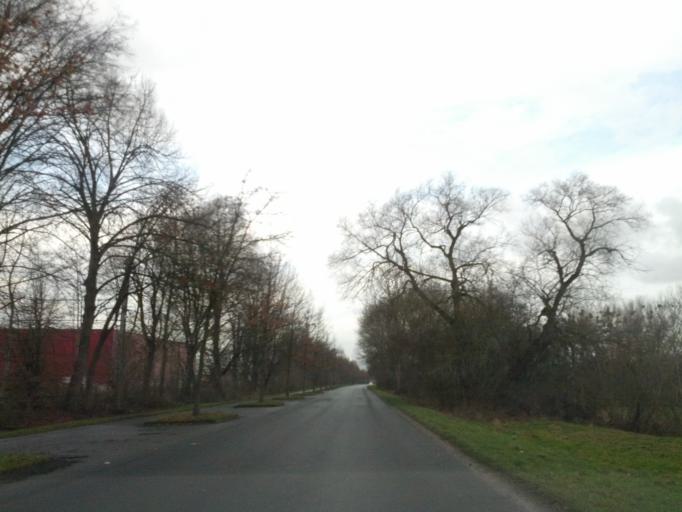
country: DE
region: Hesse
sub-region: Regierungsbezirk Kassel
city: Kaufungen
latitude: 51.2866
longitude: 9.5807
